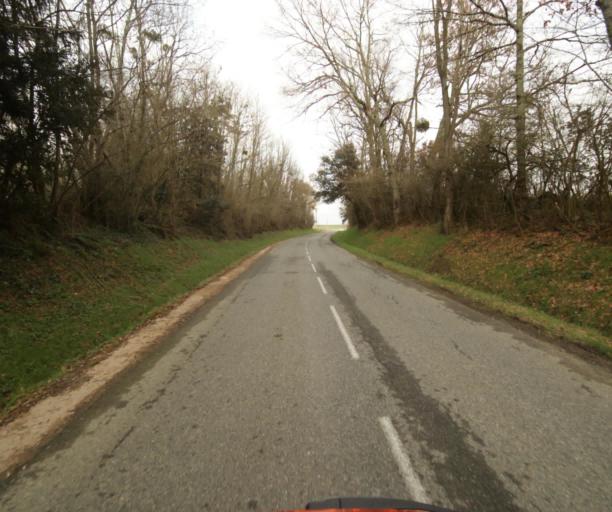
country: FR
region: Midi-Pyrenees
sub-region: Departement de l'Ariege
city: Pamiers
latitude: 43.1110
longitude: 1.5471
